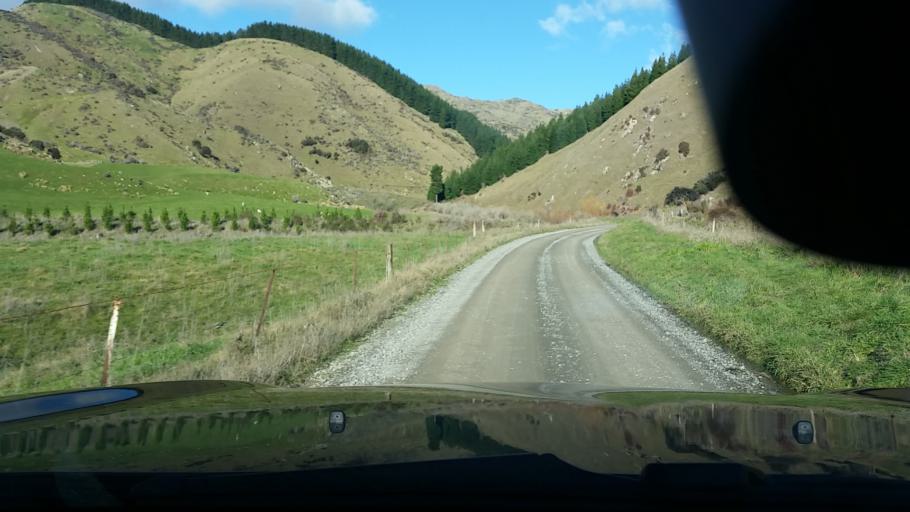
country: NZ
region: Marlborough
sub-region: Marlborough District
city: Blenheim
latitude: -41.6040
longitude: 173.9736
